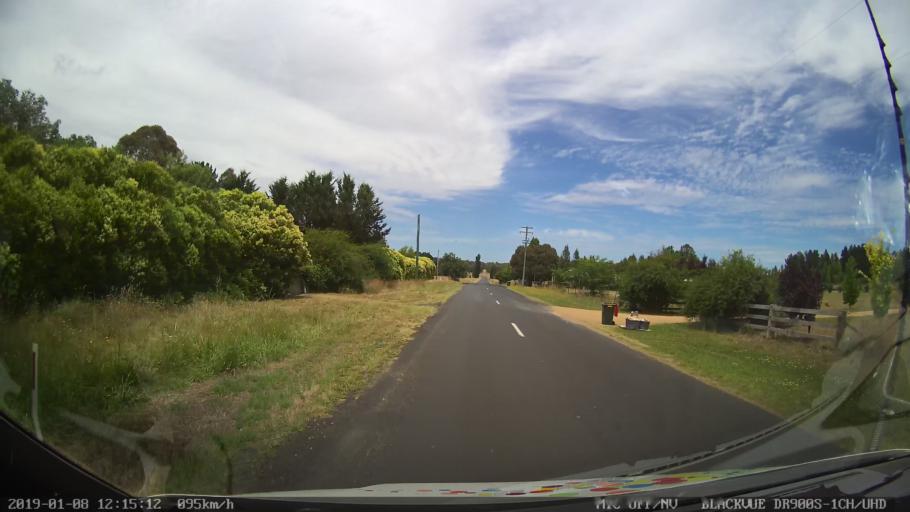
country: AU
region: New South Wales
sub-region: Armidale Dumaresq
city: Armidale
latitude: -30.4849
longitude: 151.6287
